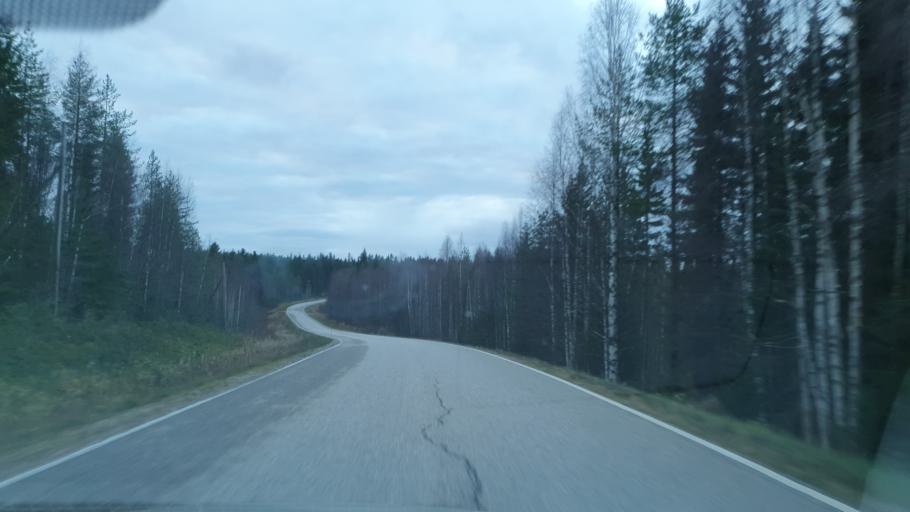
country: FI
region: Kainuu
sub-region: Kajaani
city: Ristijaervi
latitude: 64.4277
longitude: 28.3873
